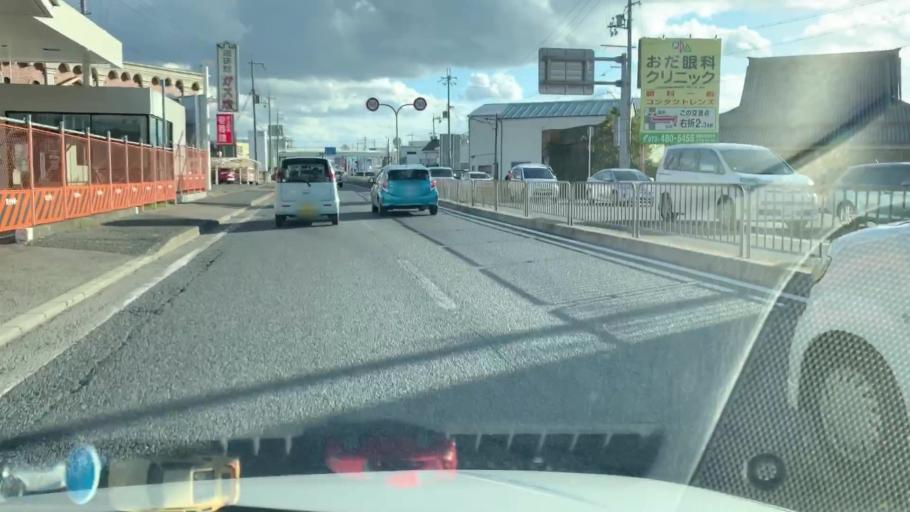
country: JP
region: Wakayama
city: Wakayama-shi
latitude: 34.2481
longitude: 135.1498
